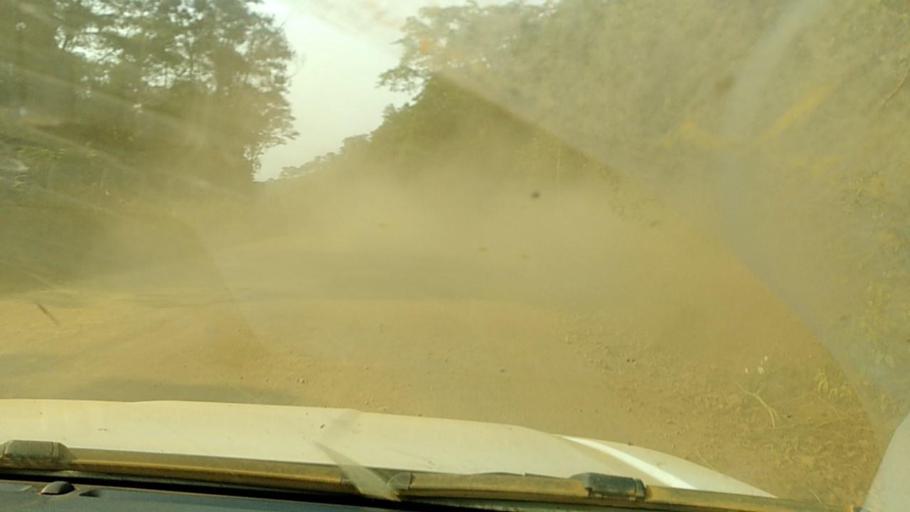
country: BR
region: Rondonia
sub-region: Porto Velho
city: Porto Velho
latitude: -8.7513
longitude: -63.9640
